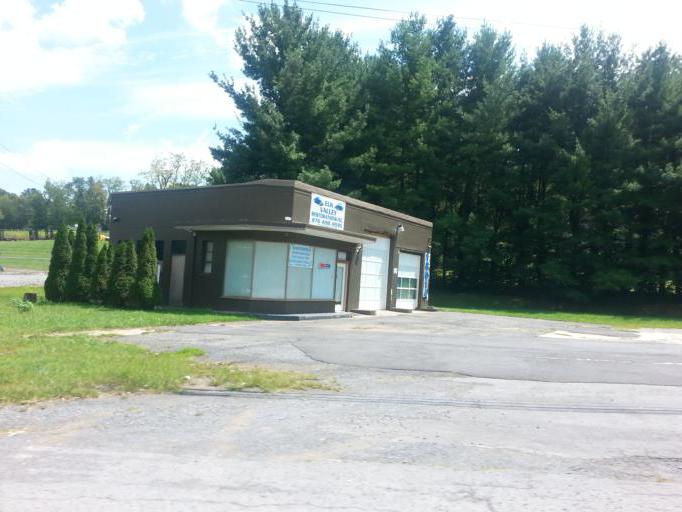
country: US
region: Virginia
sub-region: Washington County
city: Abingdon
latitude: 36.6757
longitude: -82.0465
